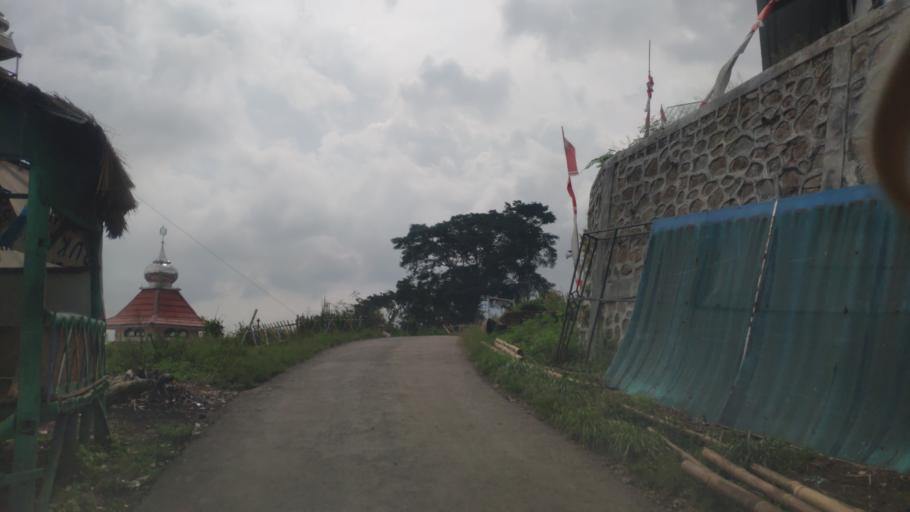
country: ID
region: Central Java
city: Wonosobo
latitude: -7.2467
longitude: 109.7948
